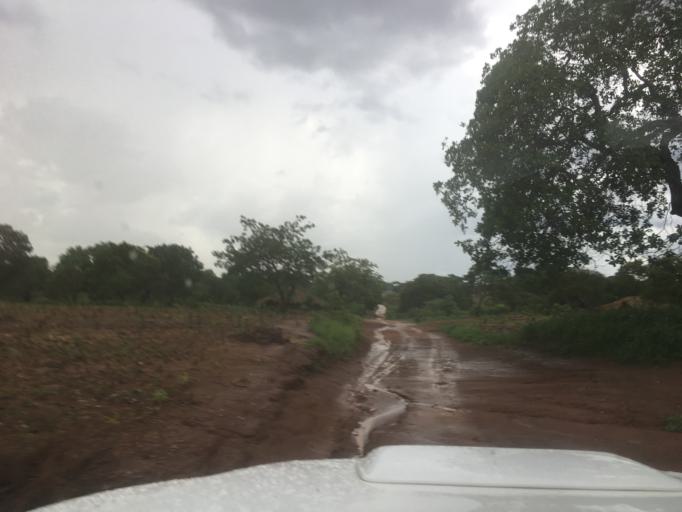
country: MZ
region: Nampula
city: Nacala
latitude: -14.7539
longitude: 39.9948
